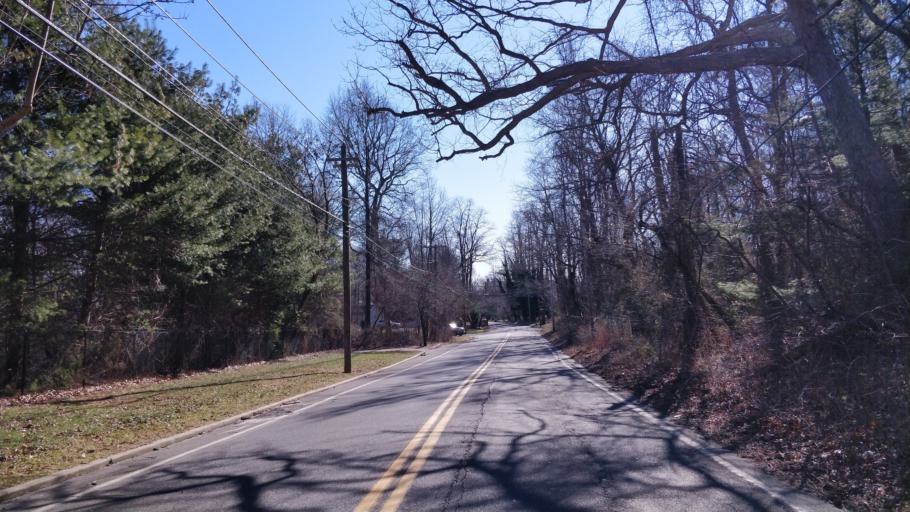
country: US
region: New York
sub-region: Suffolk County
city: Setauket-East Setauket
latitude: 40.9058
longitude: -73.1005
